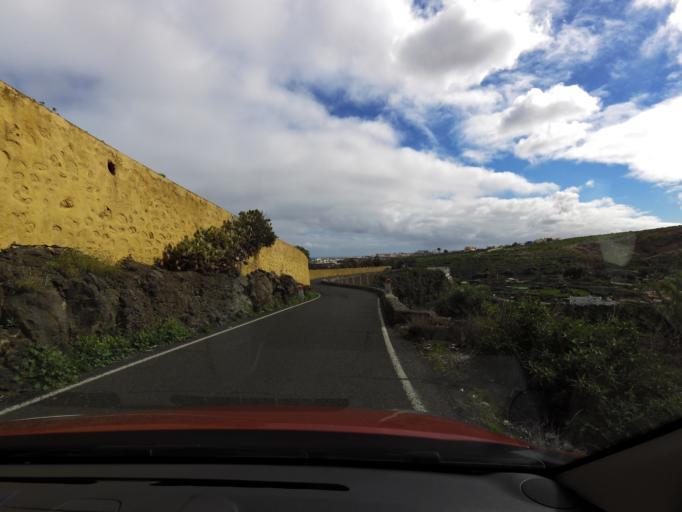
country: ES
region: Canary Islands
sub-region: Provincia de Las Palmas
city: Telde
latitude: 28.0090
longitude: -15.4293
